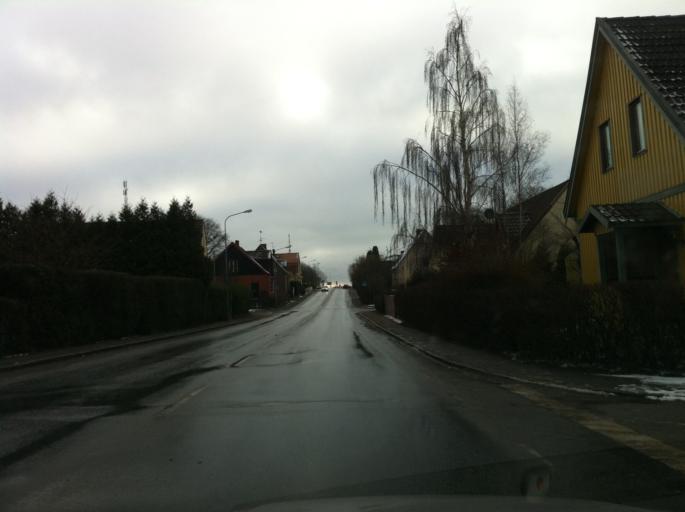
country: SE
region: Skane
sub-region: Svalovs Kommun
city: Svaloev
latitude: 55.9118
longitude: 13.1067
